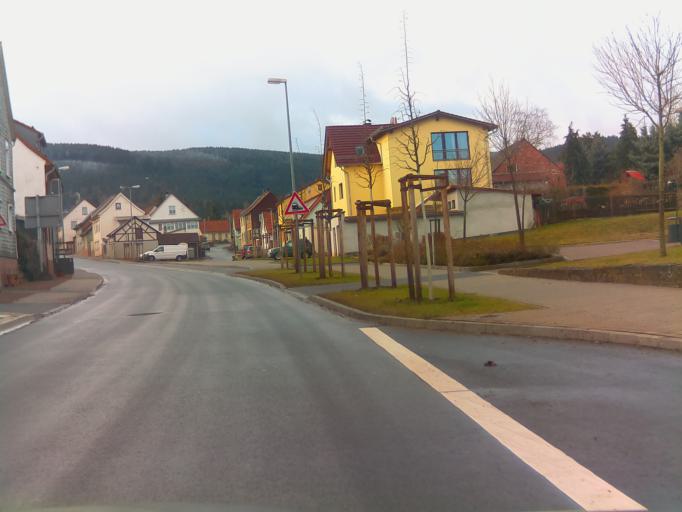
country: DE
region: Thuringia
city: Crawinkel
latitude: 50.7805
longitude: 10.7841
